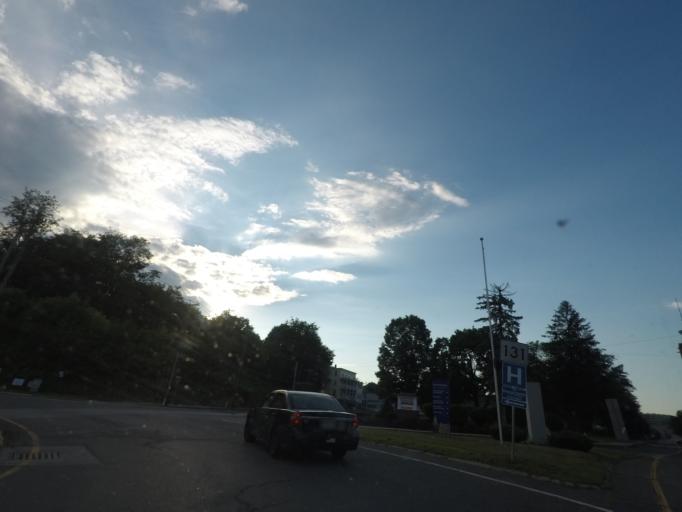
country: US
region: Massachusetts
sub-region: Worcester County
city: Southbridge
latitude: 42.0736
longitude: -72.0262
